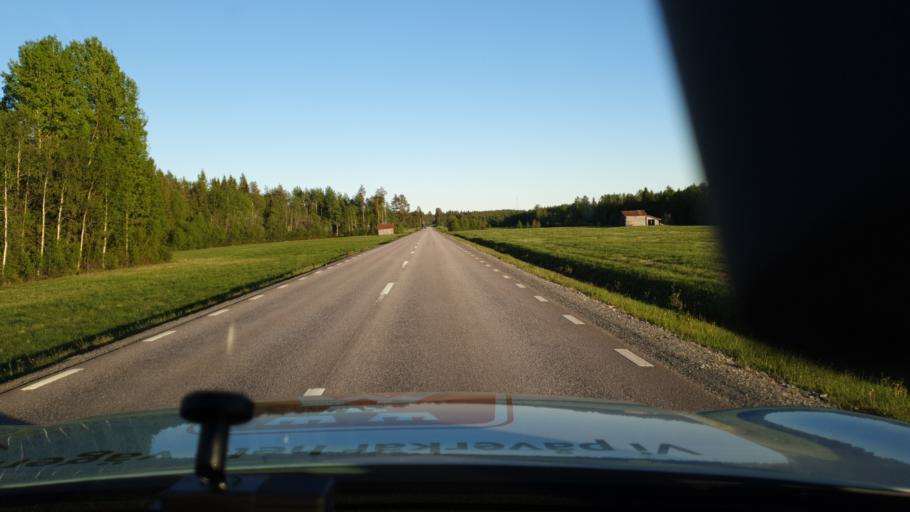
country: SE
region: Vaesterbotten
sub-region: Umea Kommun
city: Ersmark
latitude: 63.9163
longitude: 20.3080
